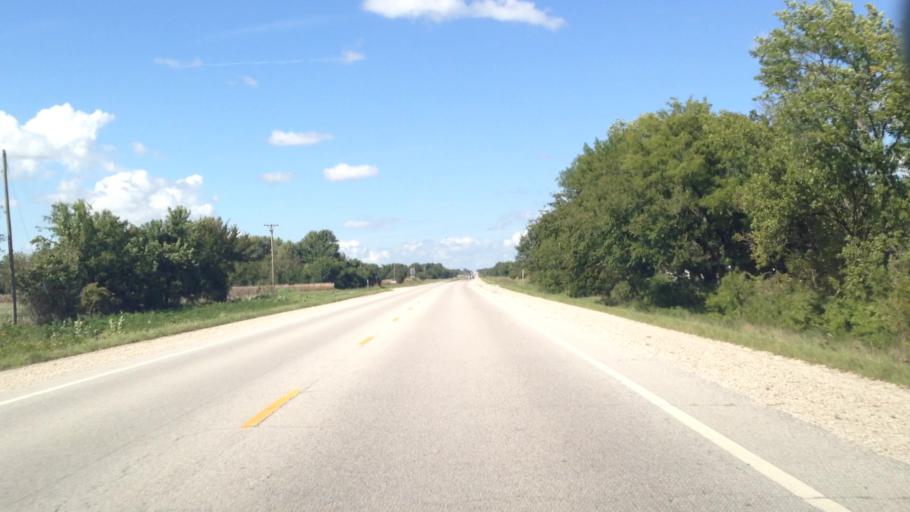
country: US
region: Kansas
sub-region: Labette County
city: Parsons
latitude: 37.4408
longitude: -95.2702
